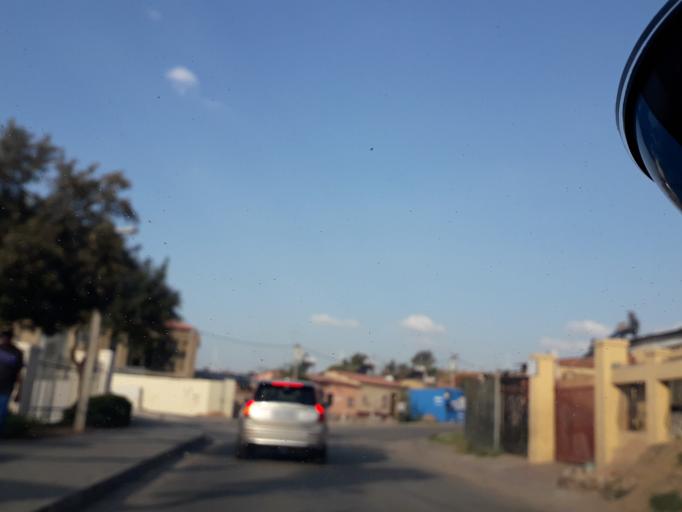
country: ZA
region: Gauteng
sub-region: City of Johannesburg Metropolitan Municipality
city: Modderfontein
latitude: -26.0842
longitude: 28.1121
